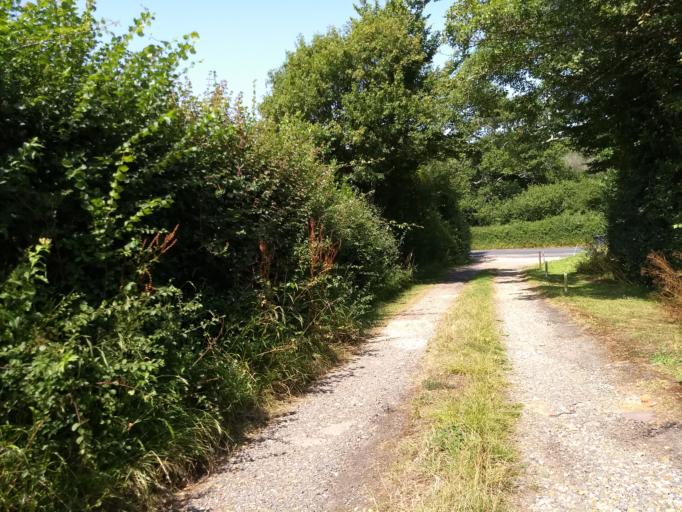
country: GB
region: England
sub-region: Isle of Wight
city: Northwood
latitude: 50.7323
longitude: -1.3339
